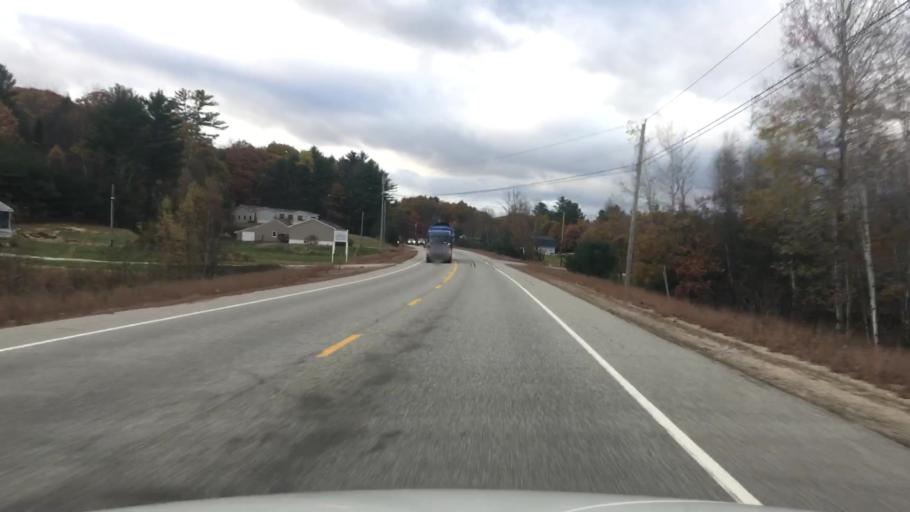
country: US
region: Maine
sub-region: Androscoggin County
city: Livermore
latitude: 44.4119
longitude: -70.2809
